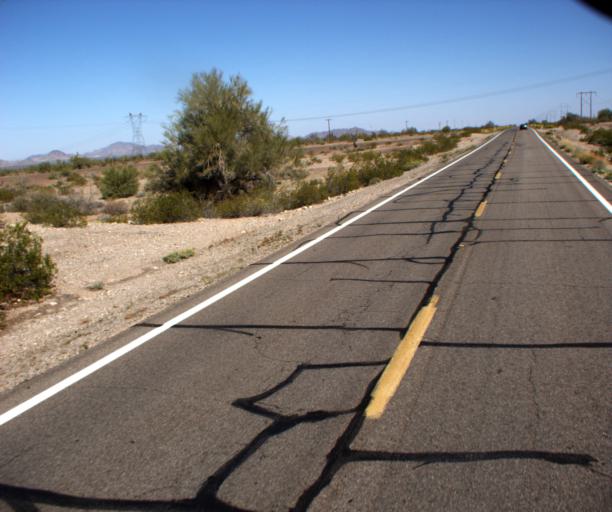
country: US
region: Arizona
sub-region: La Paz County
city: Quartzsite
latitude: 33.5395
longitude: -114.2170
